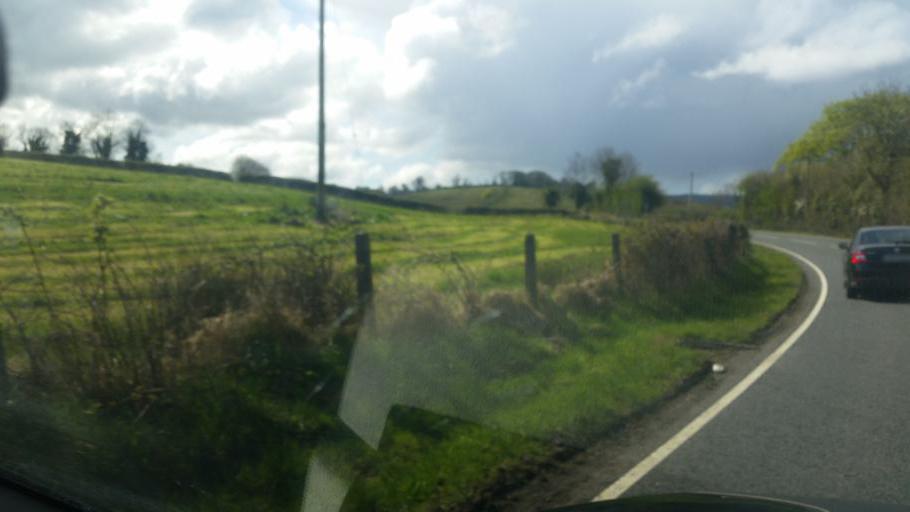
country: GB
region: Northern Ireland
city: Irvinestown
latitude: 54.4521
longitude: -7.8084
